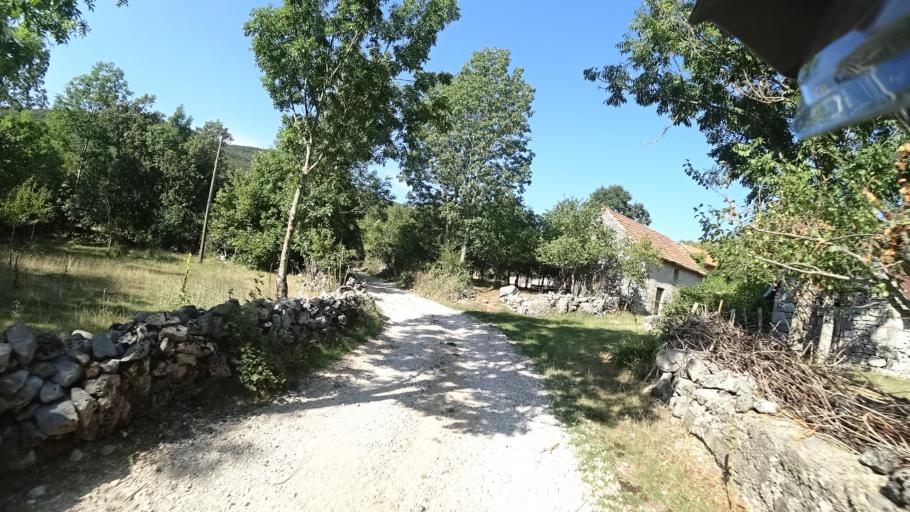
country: HR
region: Zadarska
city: Gracac
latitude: 44.2996
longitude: 16.0221
